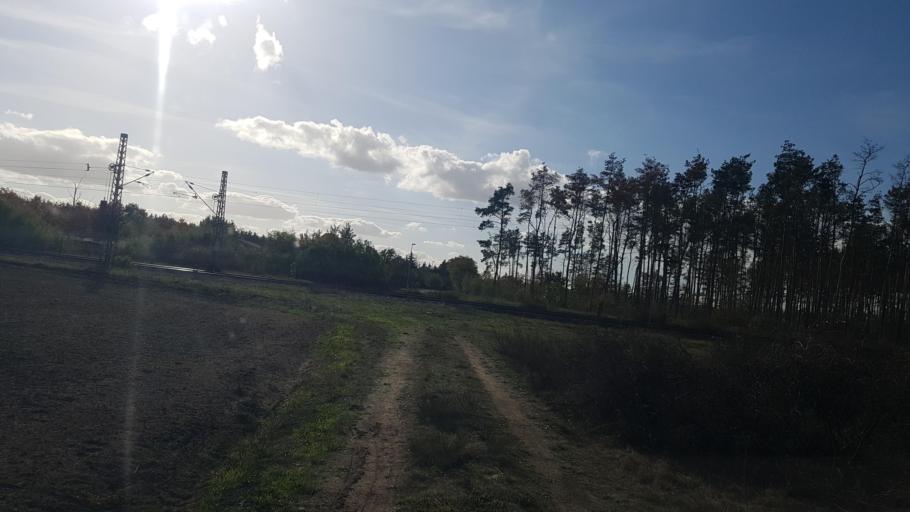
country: DE
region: Brandenburg
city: Muhlberg
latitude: 51.4481
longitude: 13.3021
